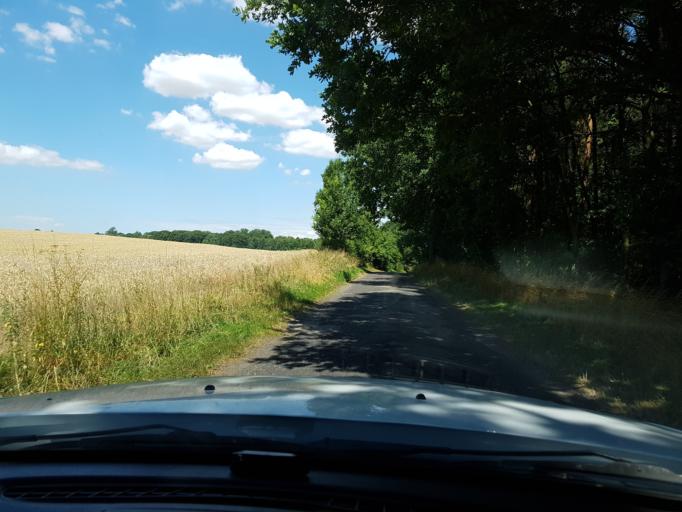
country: PL
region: West Pomeranian Voivodeship
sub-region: Powiat mysliborski
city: Barlinek
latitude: 52.9777
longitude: 15.1284
